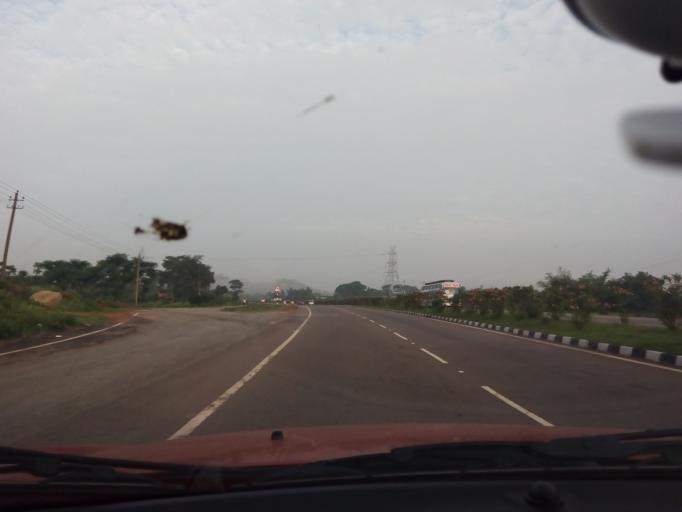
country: IN
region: Karnataka
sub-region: Ramanagara
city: Magadi
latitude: 13.0761
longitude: 77.2073
